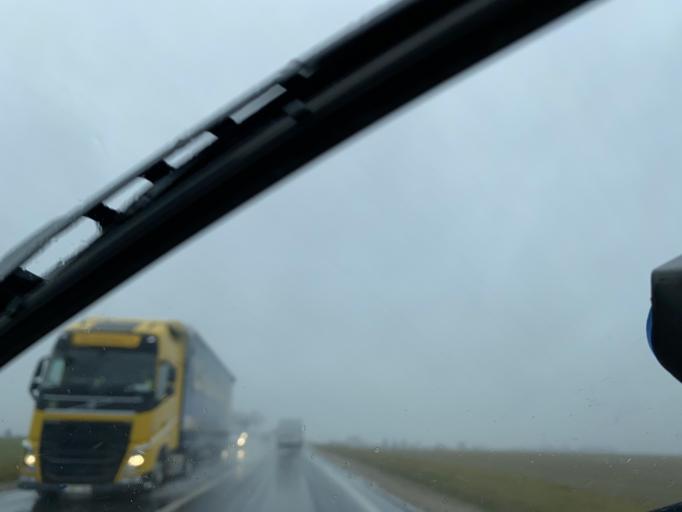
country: FR
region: Centre
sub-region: Departement d'Eure-et-Loir
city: Mainvilliers
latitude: 48.4432
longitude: 1.4330
